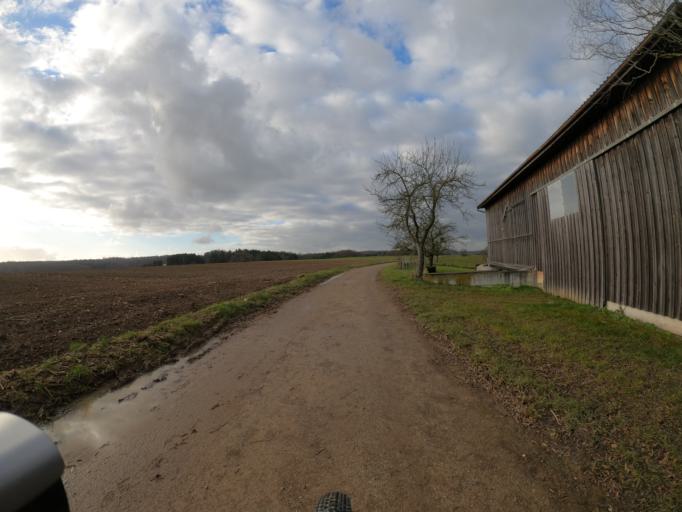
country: DE
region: Baden-Wuerttemberg
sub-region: Regierungsbezirk Stuttgart
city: Schlierbach
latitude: 48.6752
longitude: 9.4995
